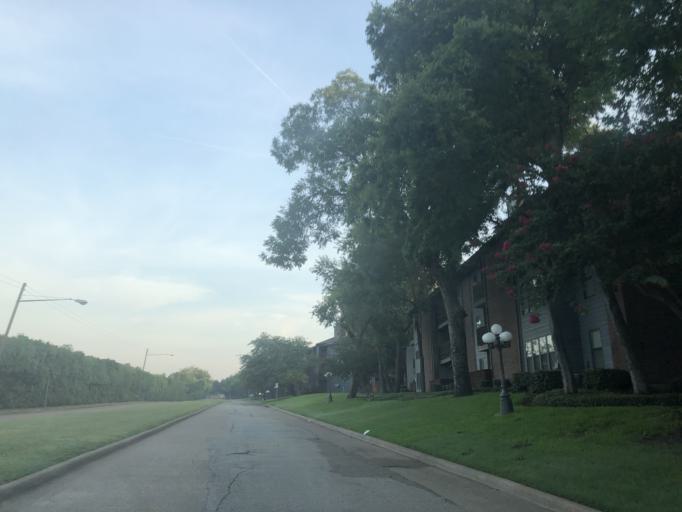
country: US
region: Texas
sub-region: Dallas County
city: Garland
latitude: 32.8444
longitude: -96.6373
